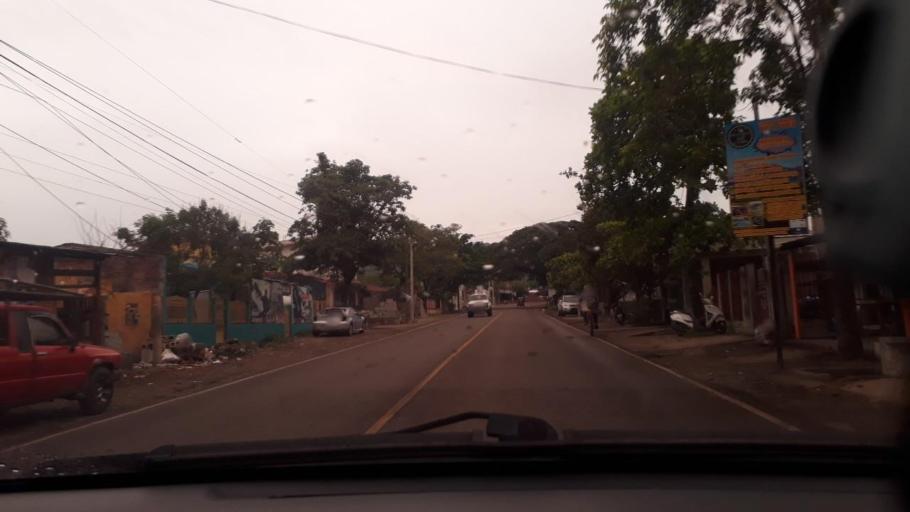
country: GT
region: Jutiapa
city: Atescatempa
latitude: 14.1894
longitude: -89.6693
